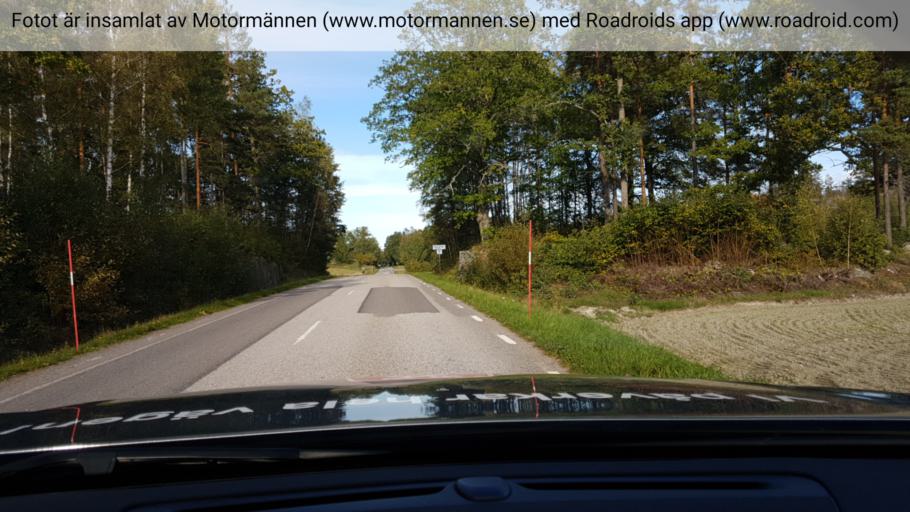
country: SE
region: Kalmar
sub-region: Vasterviks Kommun
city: Forserum
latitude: 58.0405
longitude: 16.5980
